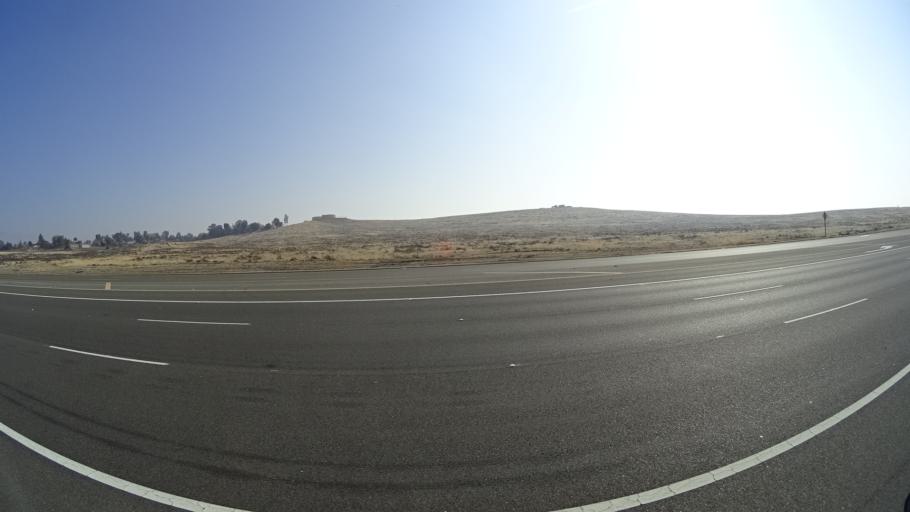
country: US
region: California
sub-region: Kern County
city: Oildale
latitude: 35.4013
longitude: -118.8758
